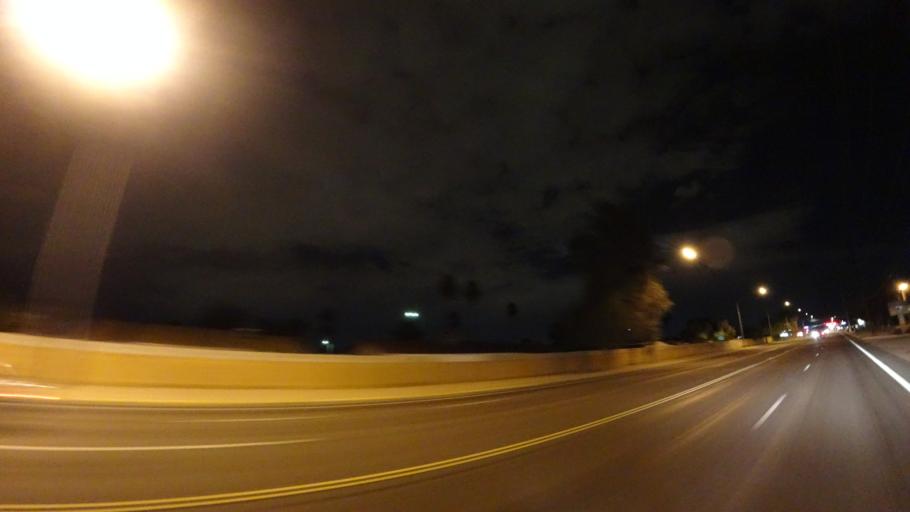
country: US
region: Arizona
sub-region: Maricopa County
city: Mesa
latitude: 33.3965
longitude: -111.8487
